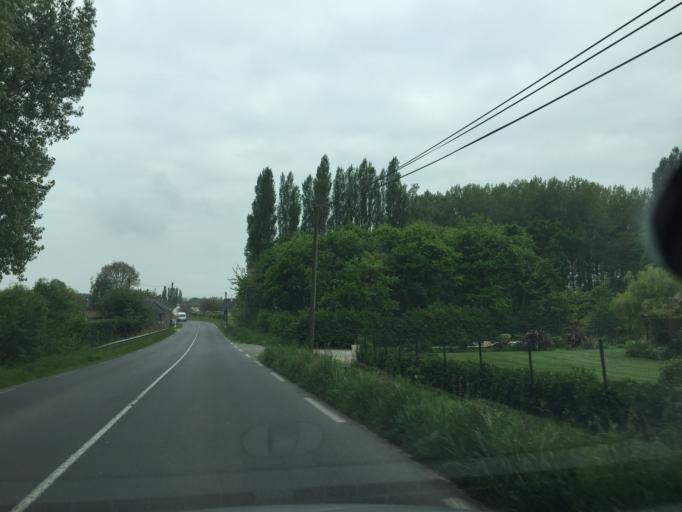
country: FR
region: Brittany
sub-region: Departement des Cotes-d'Armor
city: Matignon
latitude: 48.5860
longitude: -2.3205
